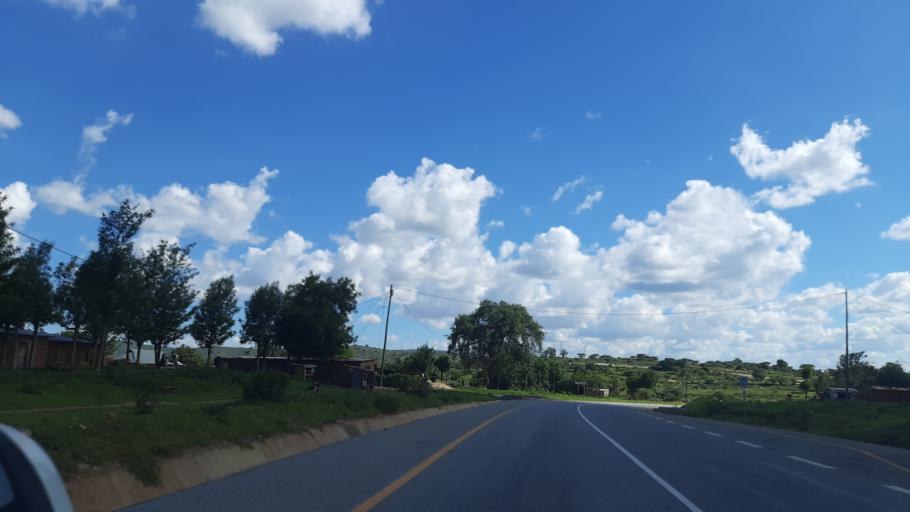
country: TZ
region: Dodoma
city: Kondoa
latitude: -4.8996
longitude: 35.8082
